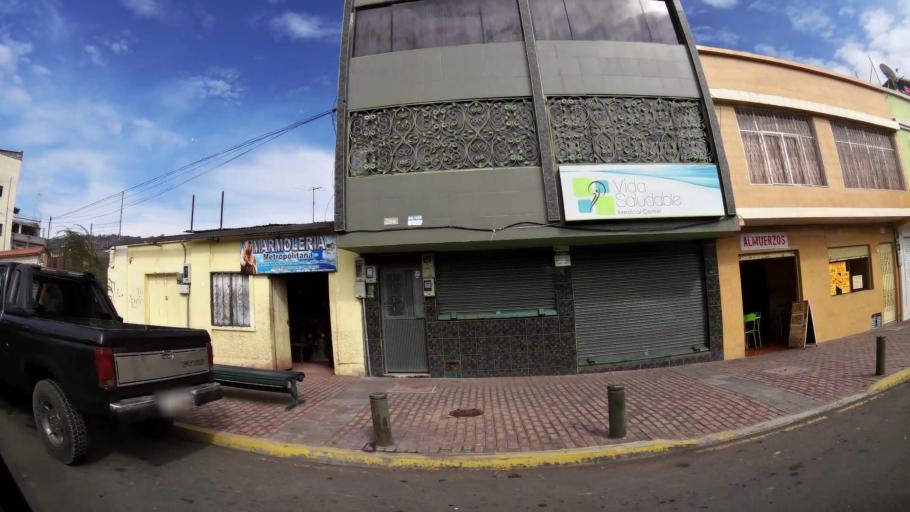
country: EC
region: Tungurahua
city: Ambato
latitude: -1.2418
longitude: -78.6296
